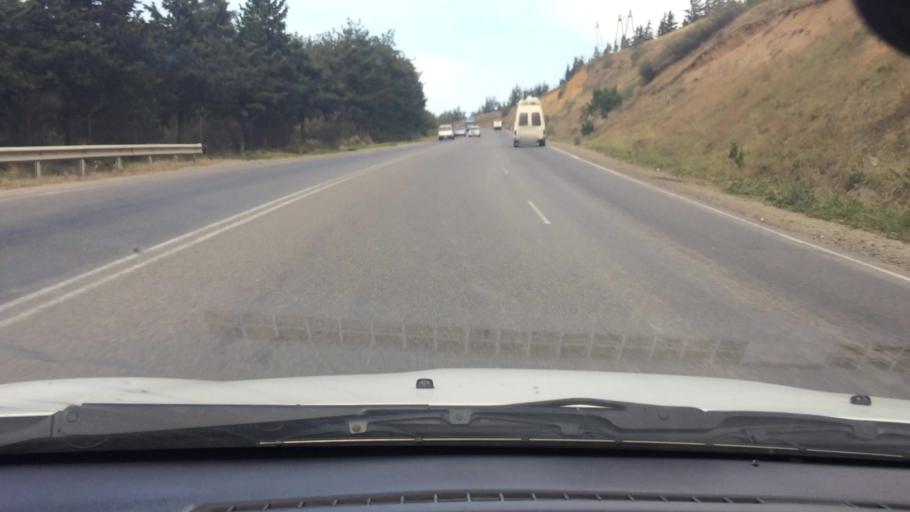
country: GE
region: T'bilisi
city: Tbilisi
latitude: 41.6240
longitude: 44.8022
